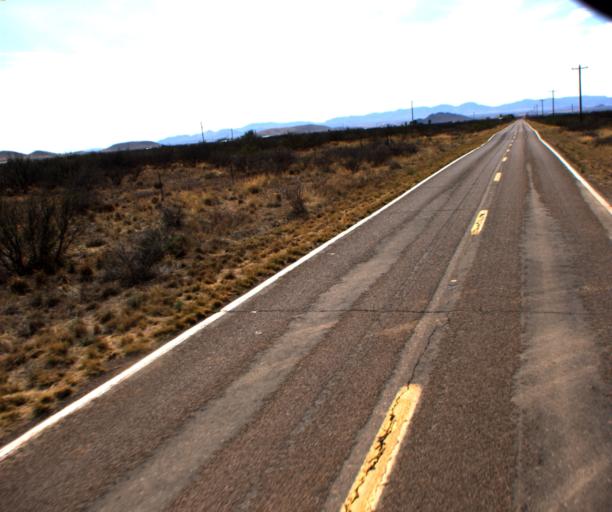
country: US
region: Arizona
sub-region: Cochise County
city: Willcox
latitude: 31.8760
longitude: -109.5614
